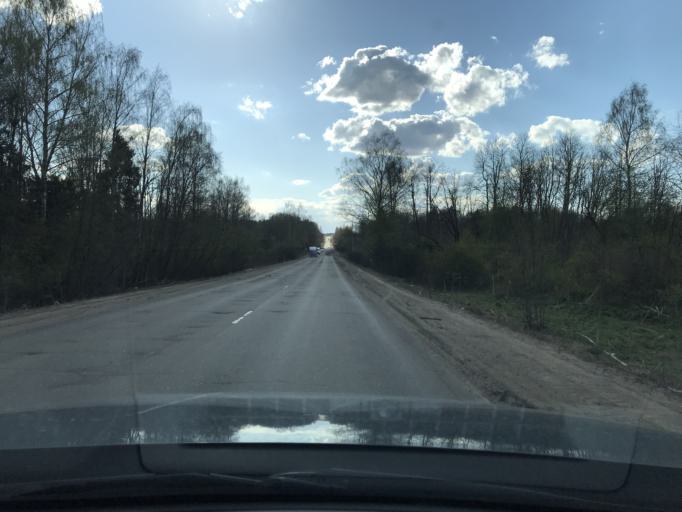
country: RU
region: Vladimir
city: Strunino
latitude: 56.4175
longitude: 38.5730
